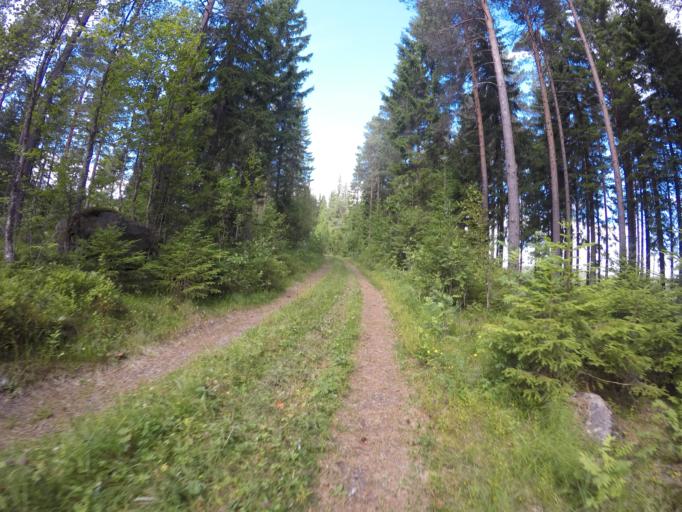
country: SE
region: Vaermland
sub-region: Filipstads Kommun
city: Lesjofors
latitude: 60.0781
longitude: 14.4577
